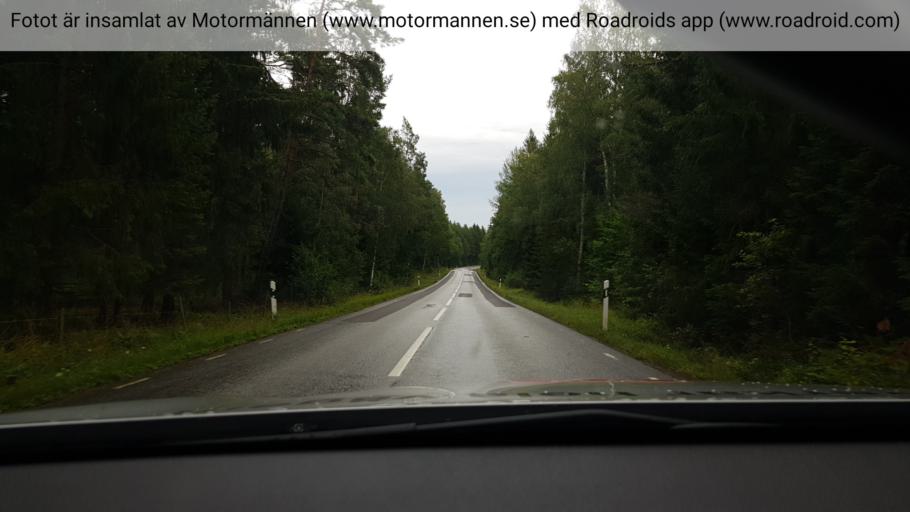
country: SE
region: Uppsala
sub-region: Osthammars Kommun
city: OEsthammar
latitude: 60.3325
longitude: 18.2303
